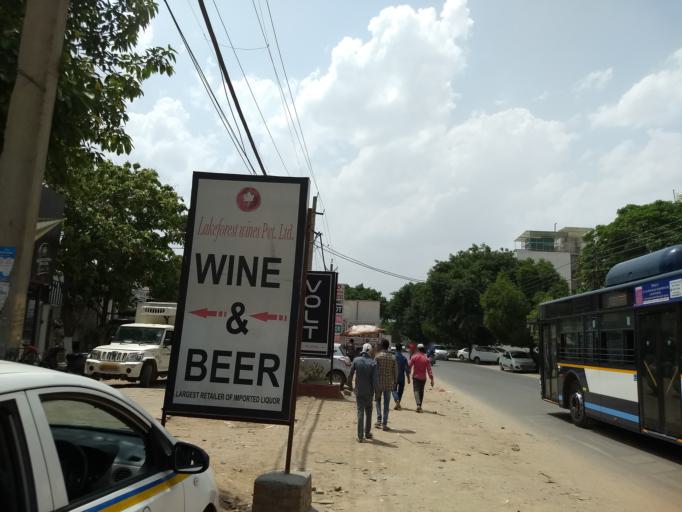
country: IN
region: Haryana
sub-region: Gurgaon
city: Gurgaon
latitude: 28.4960
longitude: 77.1026
